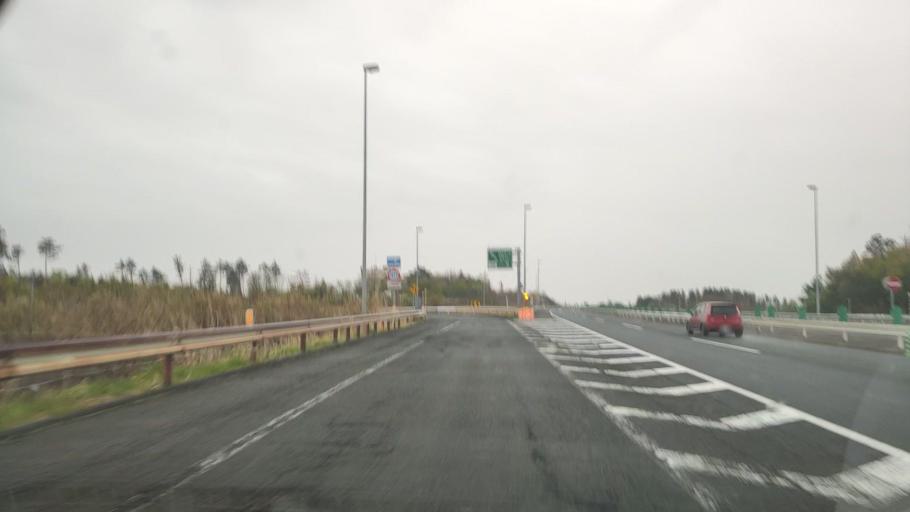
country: JP
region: Akita
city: Noshiromachi
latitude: 40.1207
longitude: 140.0120
